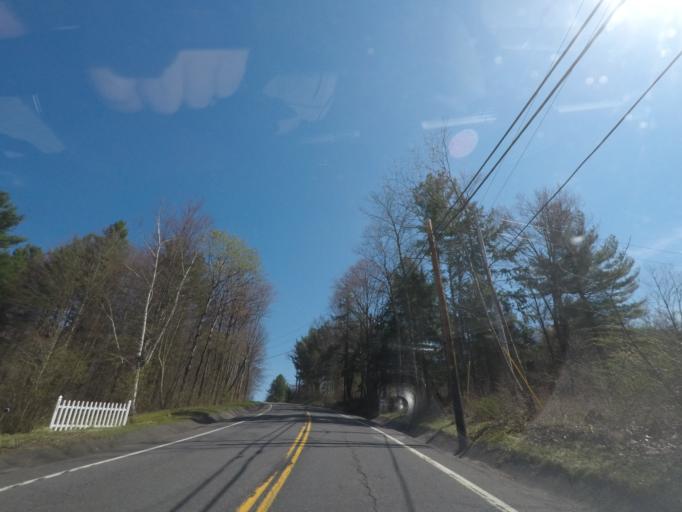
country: US
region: New York
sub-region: Rensselaer County
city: Nassau
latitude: 42.4804
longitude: -73.4724
